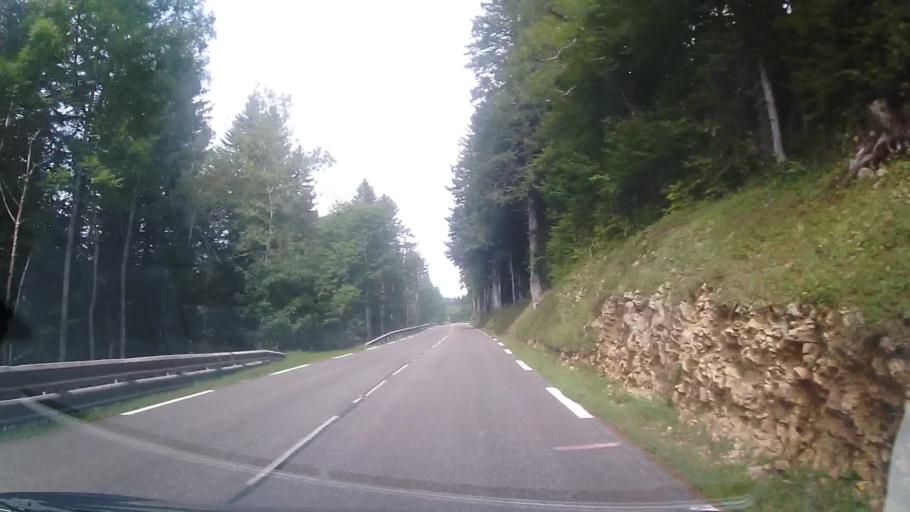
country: FR
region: Rhone-Alpes
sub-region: Departement de l'Ain
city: Gex
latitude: 46.3964
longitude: 6.0485
